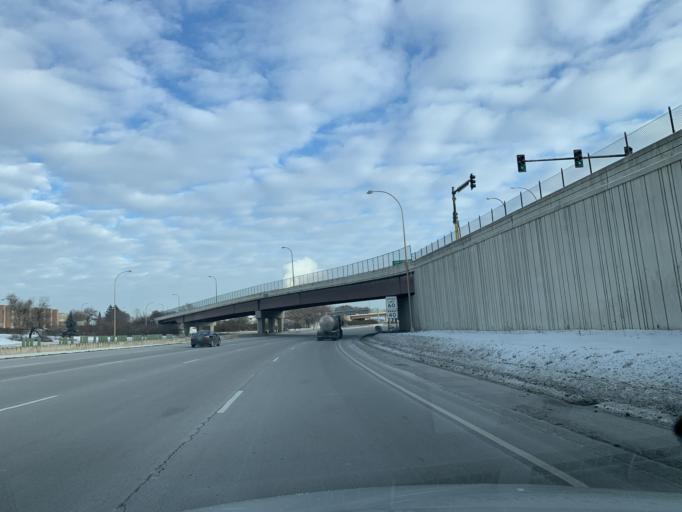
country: US
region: Minnesota
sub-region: Hennepin County
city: Minneapolis
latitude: 44.9888
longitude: -93.2882
